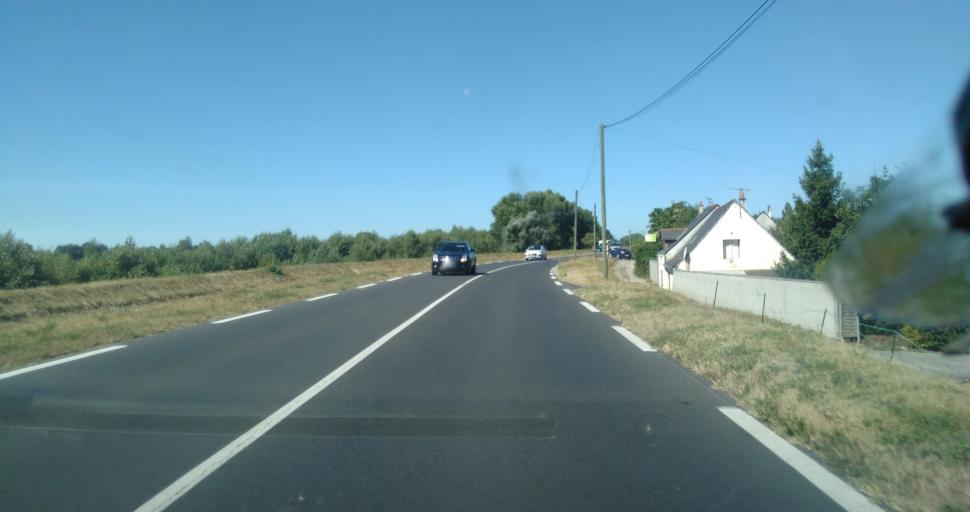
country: FR
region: Centre
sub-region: Departement d'Indre-et-Loire
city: Montlouis-sur-Loire
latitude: 47.3946
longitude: 0.8354
